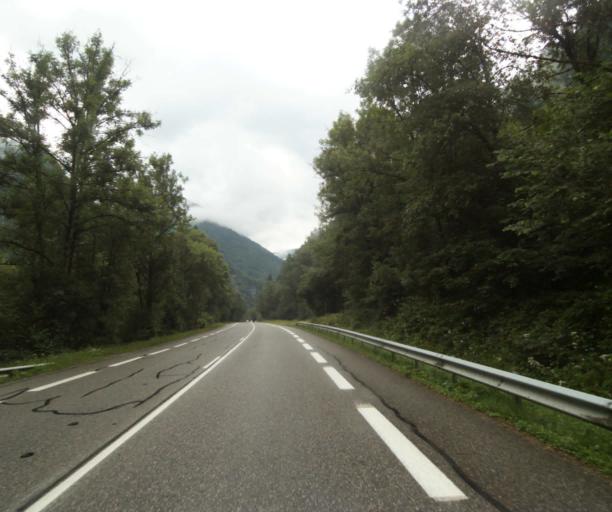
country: FR
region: Rhone-Alpes
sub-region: Departement de la Haute-Savoie
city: Thones
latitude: 45.8972
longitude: 6.2792
